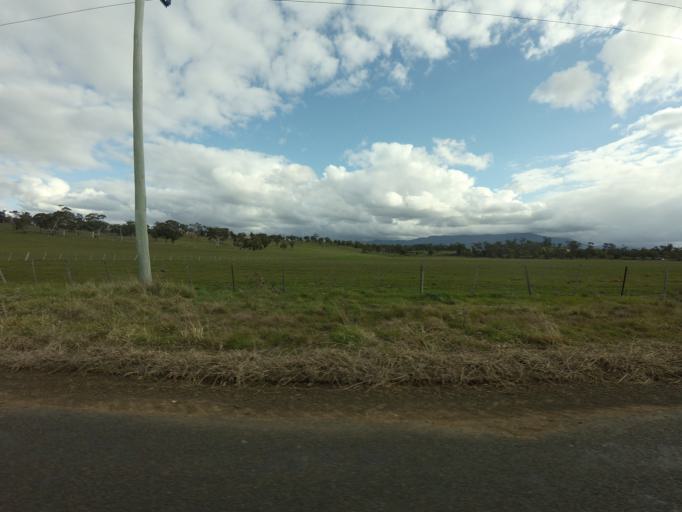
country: AU
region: Tasmania
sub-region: Northern Midlands
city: Evandale
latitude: -41.8706
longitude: 147.2949
